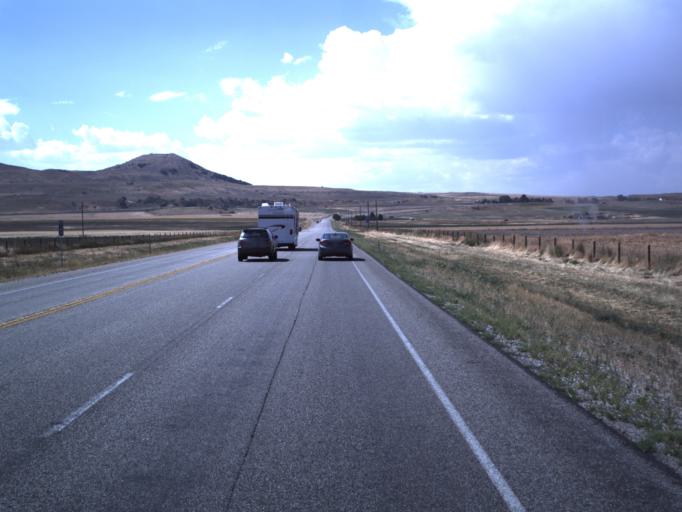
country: US
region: Utah
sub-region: Cache County
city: Mendon
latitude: 41.7523
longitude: -111.9855
